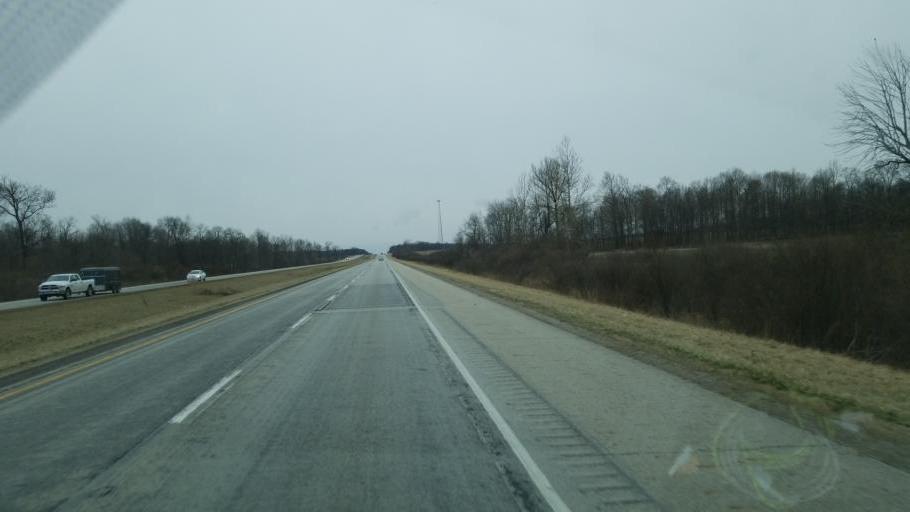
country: US
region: Indiana
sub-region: Marshall County
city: Argos
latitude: 41.1515
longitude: -86.2400
